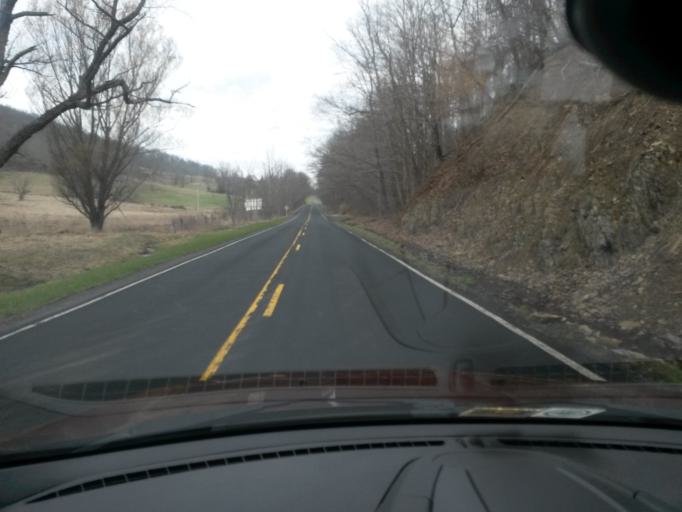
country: US
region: Virginia
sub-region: Bath County
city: Warm Springs
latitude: 38.0564
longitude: -79.7779
